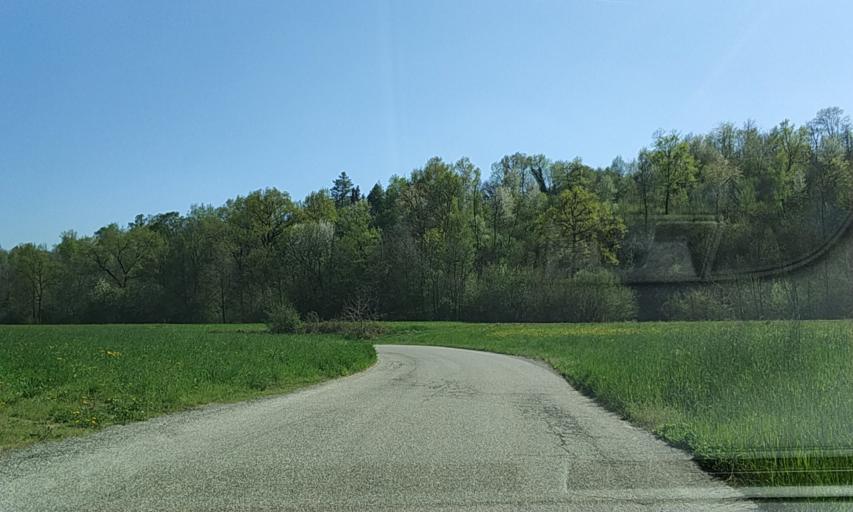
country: IT
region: Piedmont
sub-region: Provincia di Torino
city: Rivara
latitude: 45.3244
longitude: 7.6378
